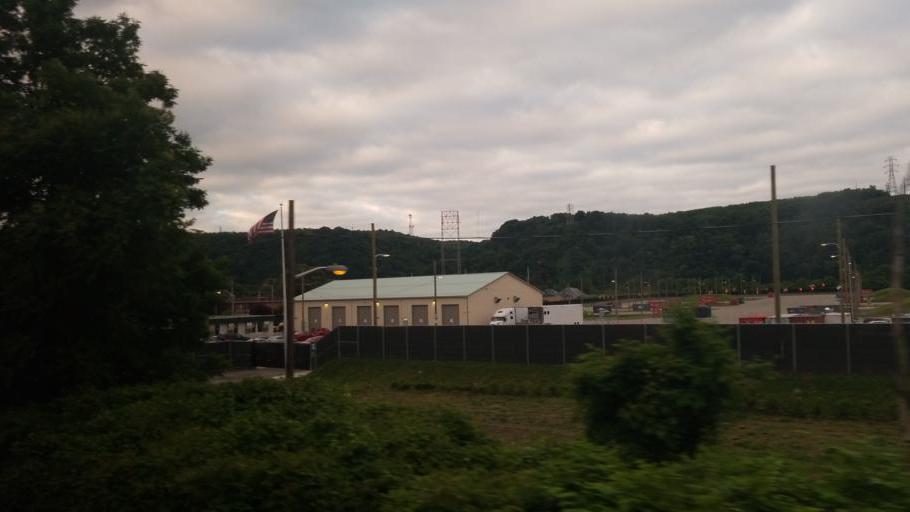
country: US
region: Pennsylvania
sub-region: Allegheny County
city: Homestead
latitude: 40.4099
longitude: -79.9447
